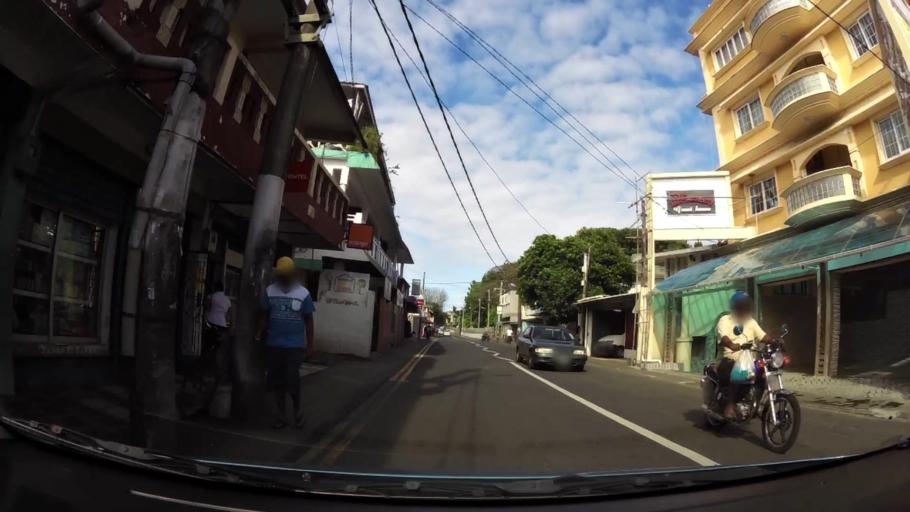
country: MU
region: Grand Port
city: Mahebourg
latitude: -20.4148
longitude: 57.7051
